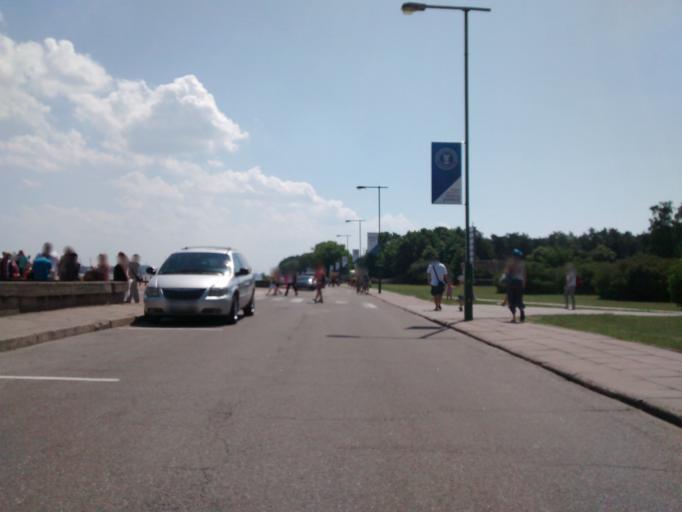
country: LT
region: Klaipedos apskritis
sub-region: Klaipeda
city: Klaipeda
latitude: 55.7156
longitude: 21.1036
